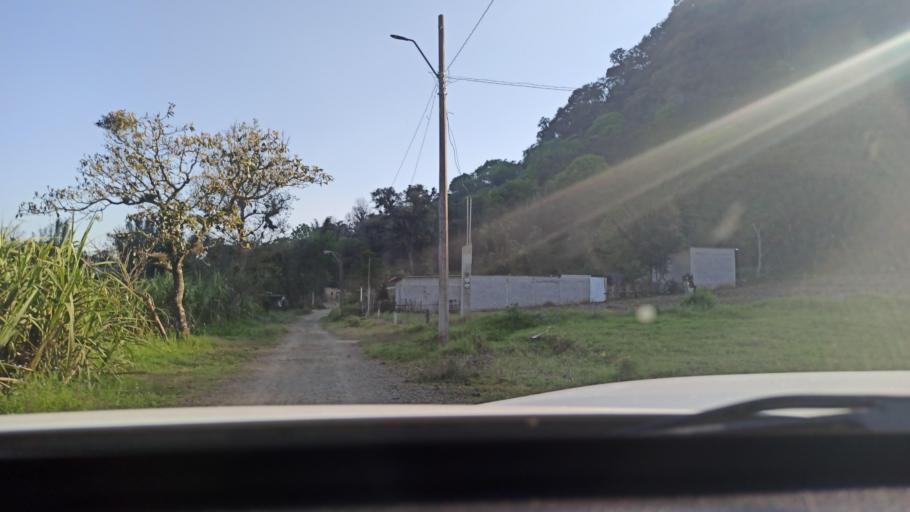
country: MX
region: Veracruz
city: Atzacan
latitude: 18.9082
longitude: -97.0904
